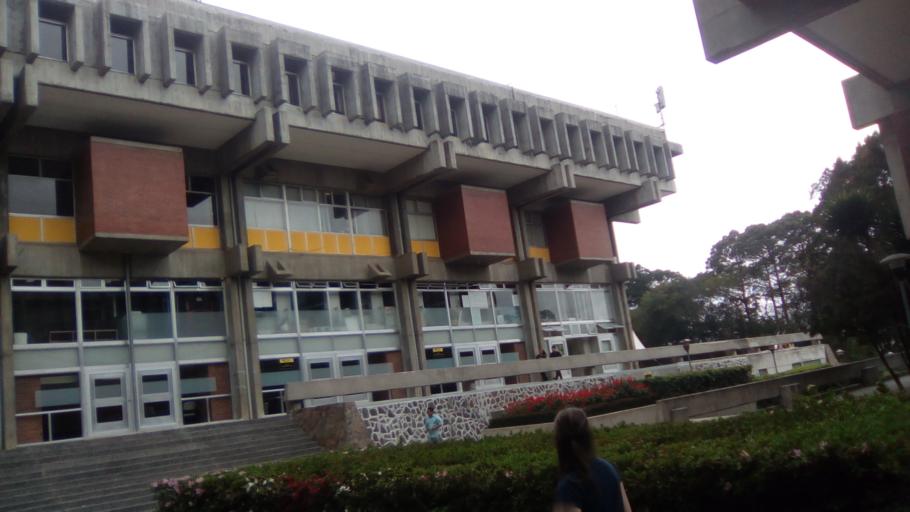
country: GT
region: Guatemala
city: Santa Catarina Pinula
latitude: 14.5953
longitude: -90.4847
